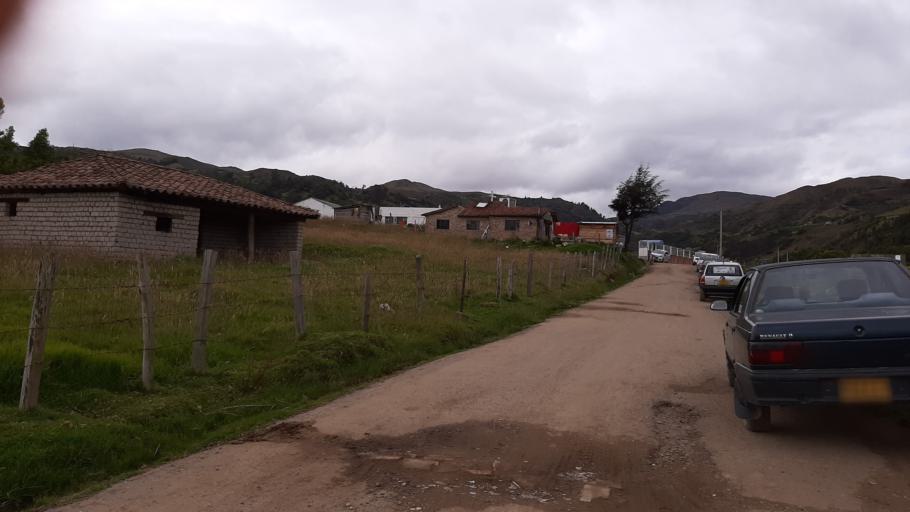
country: CO
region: Boyaca
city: Aquitania
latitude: 5.4812
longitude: -72.9460
